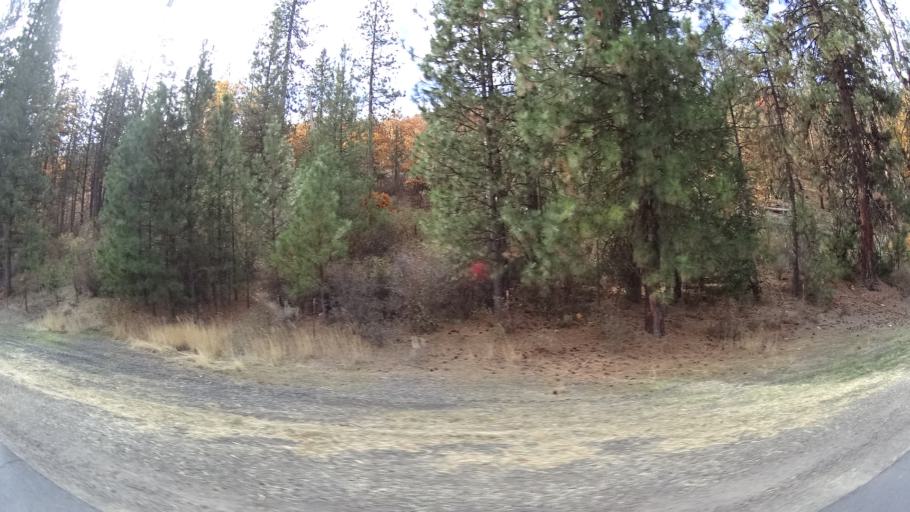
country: US
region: California
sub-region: Siskiyou County
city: Yreka
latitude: 41.6258
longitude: -122.8202
